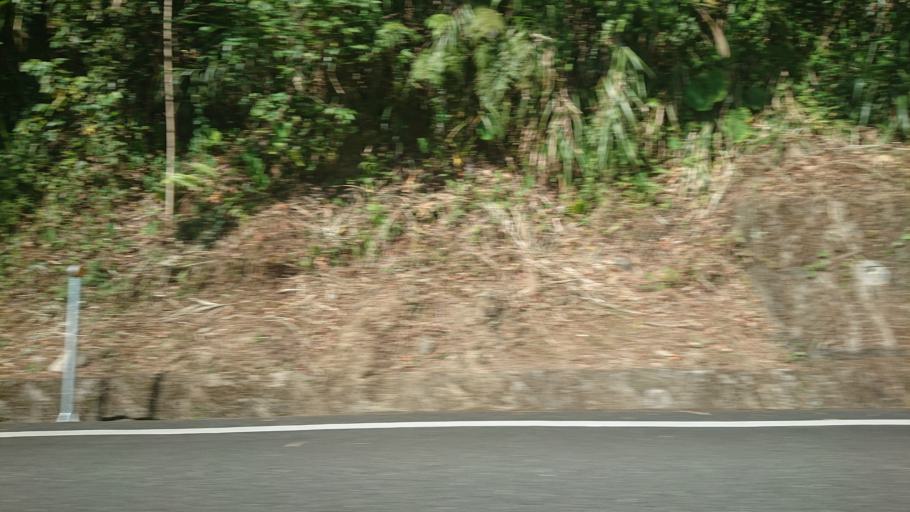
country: TW
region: Taiwan
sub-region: Chiayi
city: Jiayi Shi
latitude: 23.4604
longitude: 120.7236
